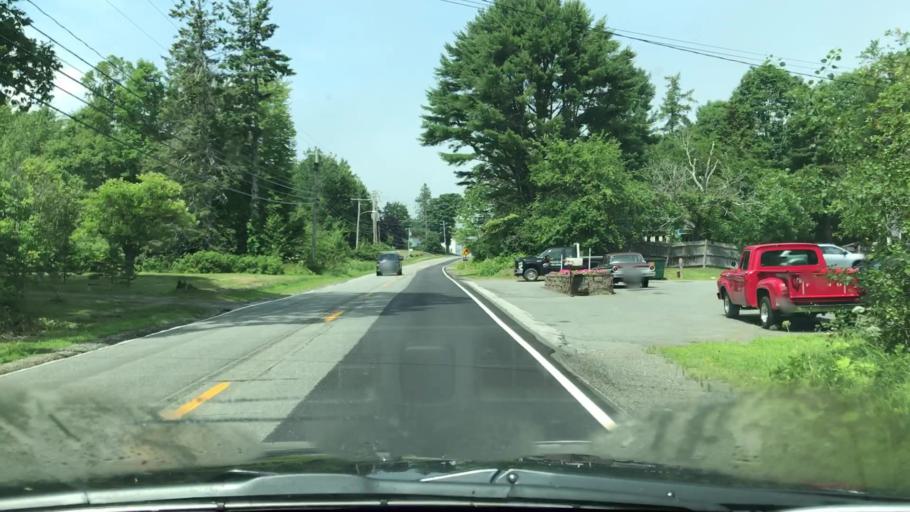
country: US
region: Maine
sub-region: Waldo County
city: Lincolnville
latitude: 44.2925
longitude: -69.0079
